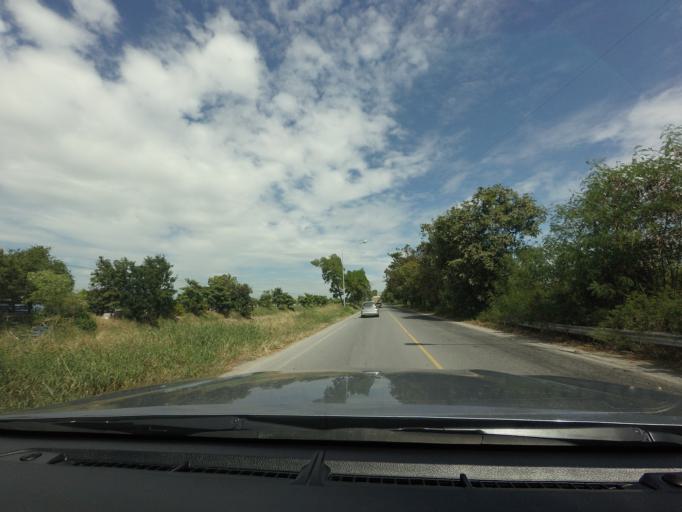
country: TH
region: Suphan Buri
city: Suphan Buri
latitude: 14.4614
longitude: 100.0890
